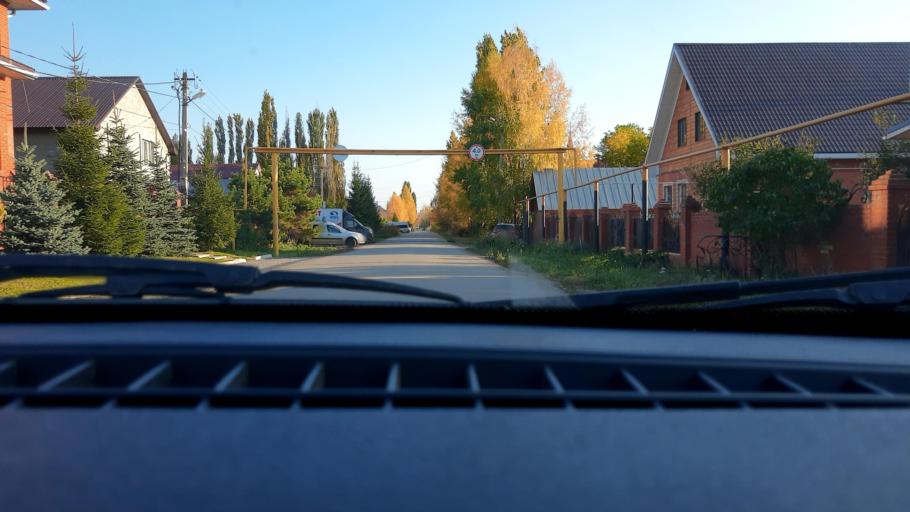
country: RU
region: Bashkortostan
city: Mikhaylovka
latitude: 54.7889
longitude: 55.8963
